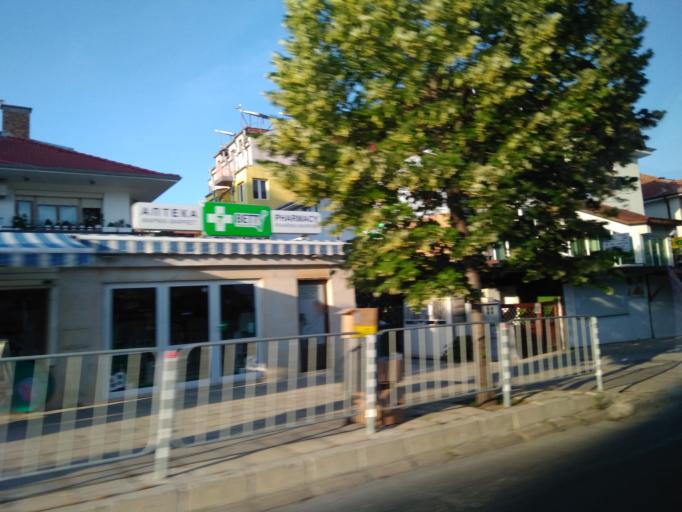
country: BG
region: Burgas
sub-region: Obshtina Nesebur
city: Nesebar
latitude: 42.6621
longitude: 27.7206
